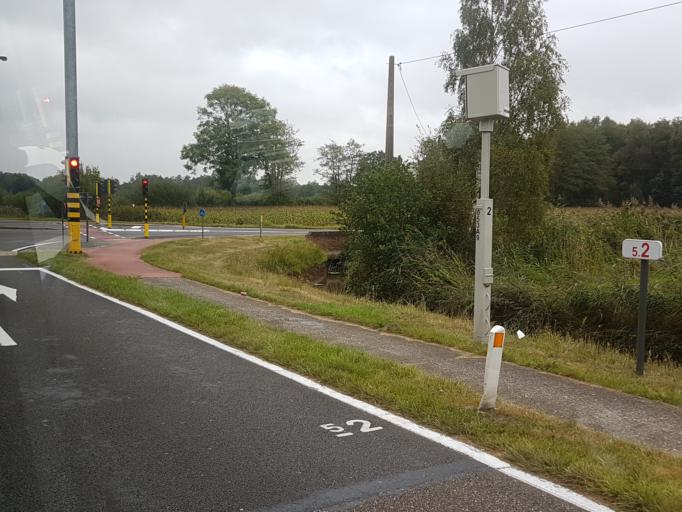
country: BE
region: Flanders
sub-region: Provincie Antwerpen
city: Meerhout
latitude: 51.1709
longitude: 5.0623
